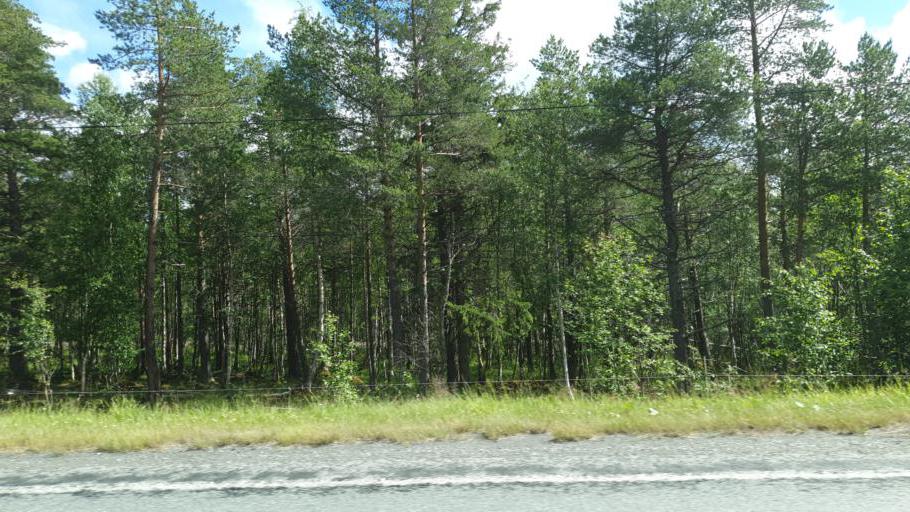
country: NO
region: Sor-Trondelag
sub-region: Rennebu
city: Berkak
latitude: 62.7033
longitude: 9.9510
